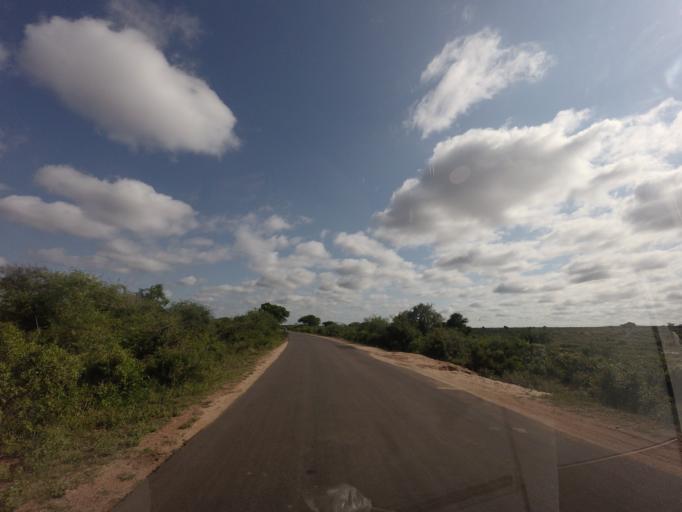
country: ZA
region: Mpumalanga
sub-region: Ehlanzeni District
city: Komatipoort
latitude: -25.1383
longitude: 31.9430
